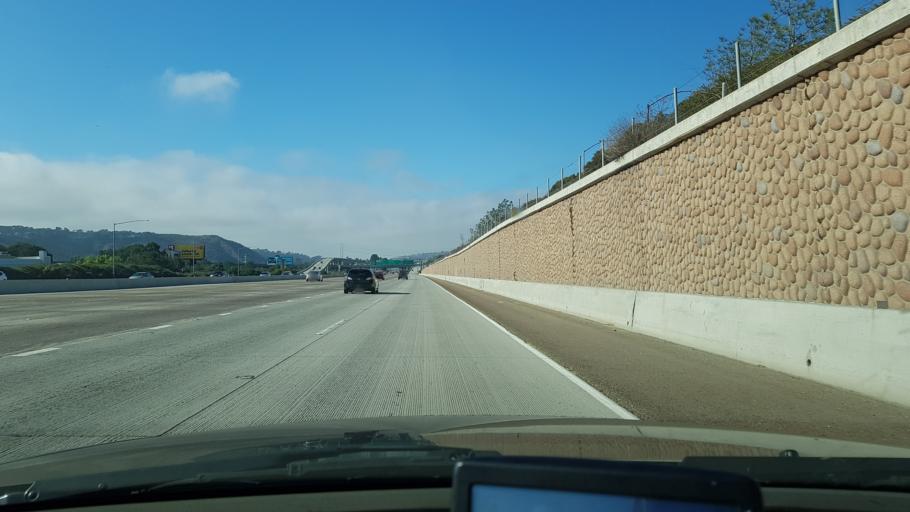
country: US
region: California
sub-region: San Diego County
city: La Jolla
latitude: 32.8977
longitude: -117.2171
